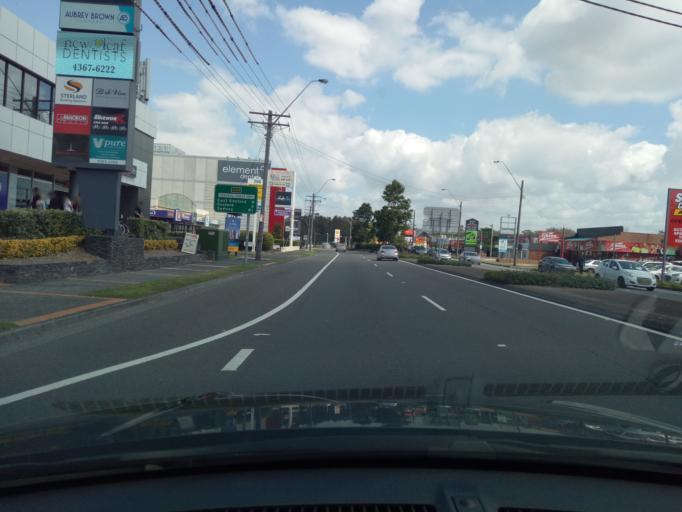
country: AU
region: New South Wales
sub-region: Gosford Shire
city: Erina
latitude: -33.4349
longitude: 151.3873
